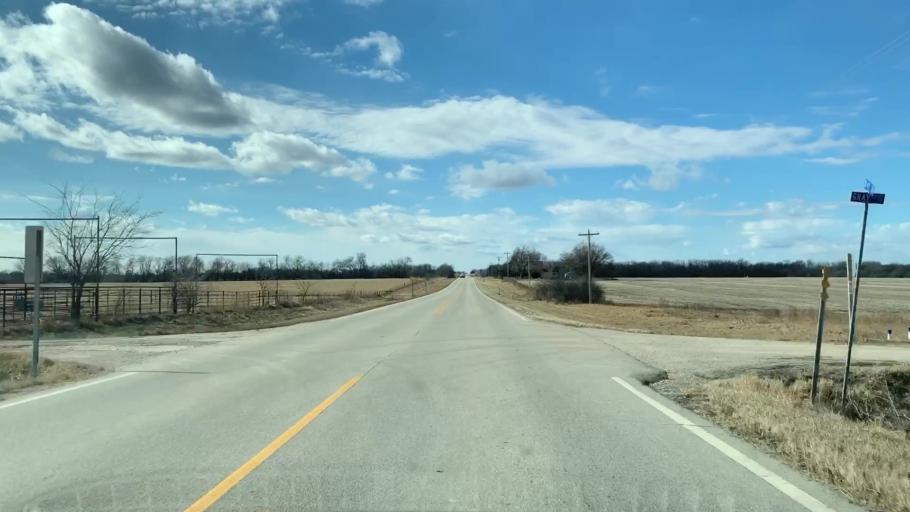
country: US
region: Kansas
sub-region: Neosho County
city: Chanute
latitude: 37.5291
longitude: -95.4159
